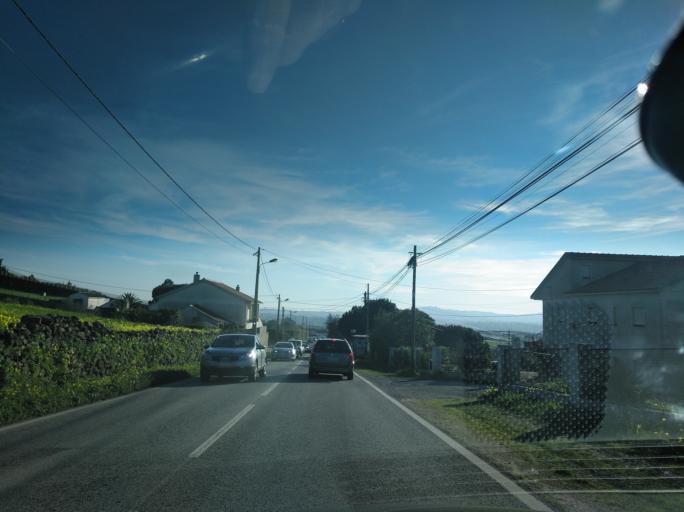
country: PT
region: Lisbon
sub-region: Mafra
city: Mafra
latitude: 38.9215
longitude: -9.3219
